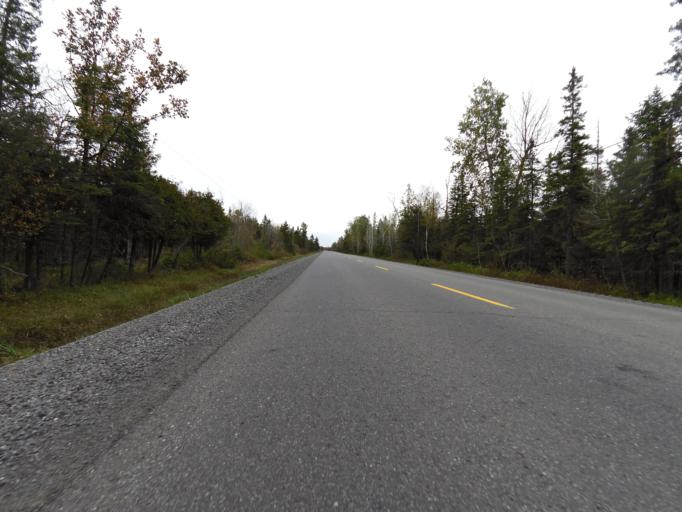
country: CA
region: Ontario
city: Brockville
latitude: 44.7931
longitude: -75.7827
